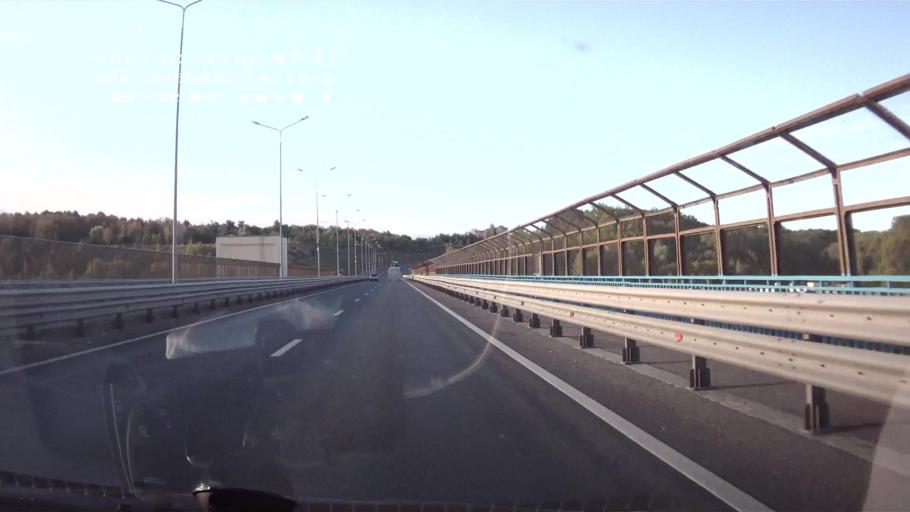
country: RU
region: Chuvashia
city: Novocheboksarsk
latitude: 56.1358
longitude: 47.4656
